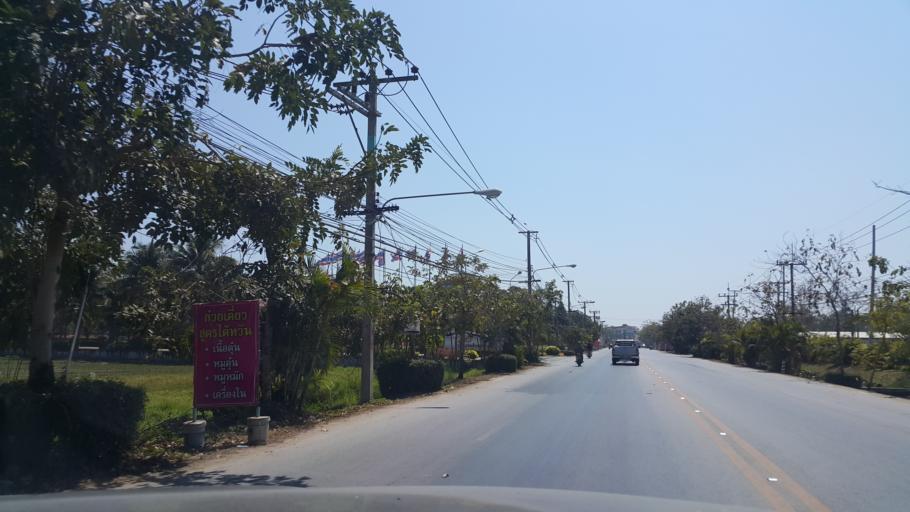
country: TH
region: Chiang Mai
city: San Sai
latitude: 18.8390
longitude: 99.0428
